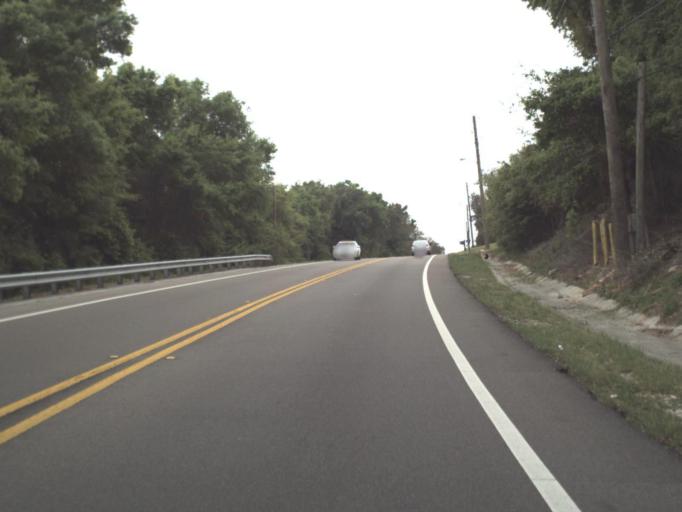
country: US
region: Florida
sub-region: Escambia County
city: East Pensacola Heights
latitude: 30.4687
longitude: -87.1612
